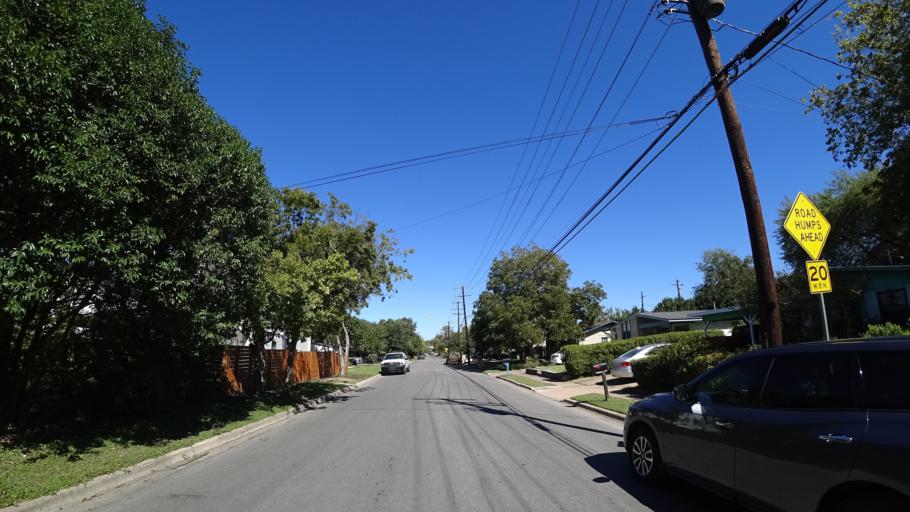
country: US
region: Texas
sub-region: Travis County
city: Austin
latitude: 30.2328
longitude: -97.7719
